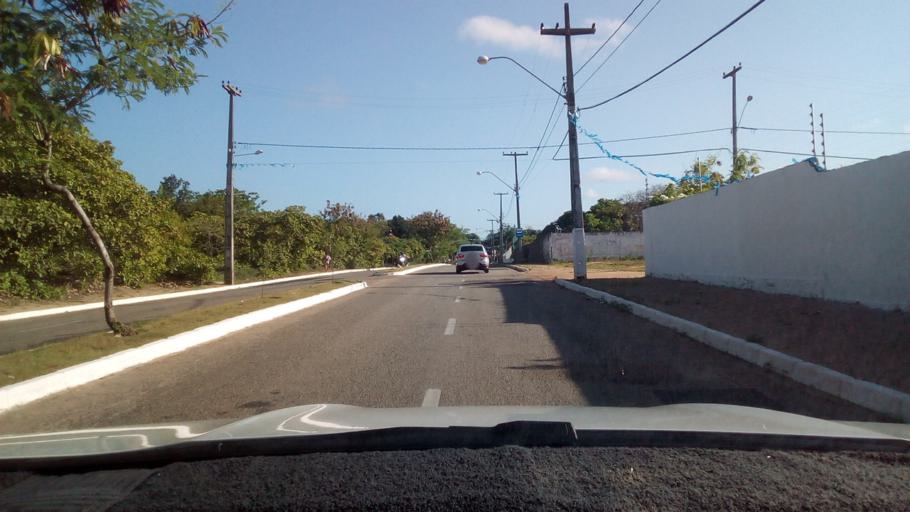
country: BR
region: Paraiba
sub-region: Joao Pessoa
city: Joao Pessoa
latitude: -7.1623
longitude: -34.7981
